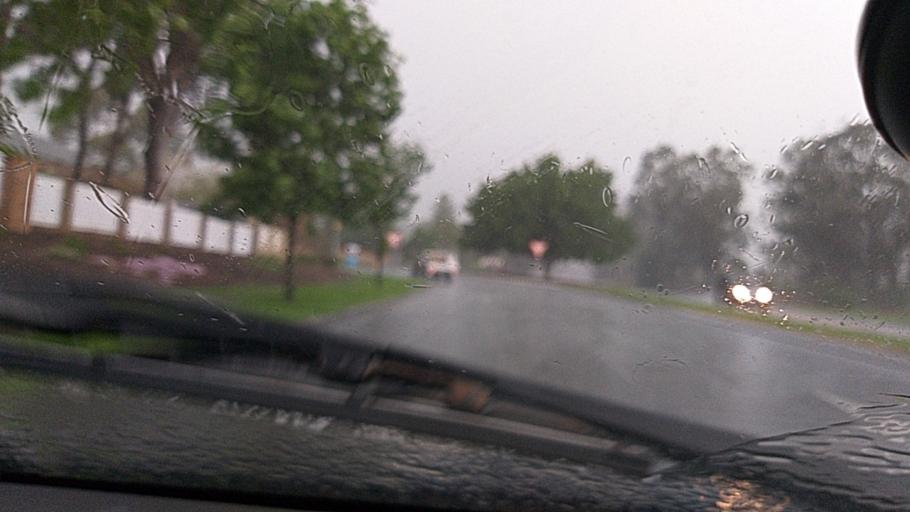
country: AU
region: New South Wales
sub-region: Camden
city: Camden South
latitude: -34.0965
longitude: 150.6950
